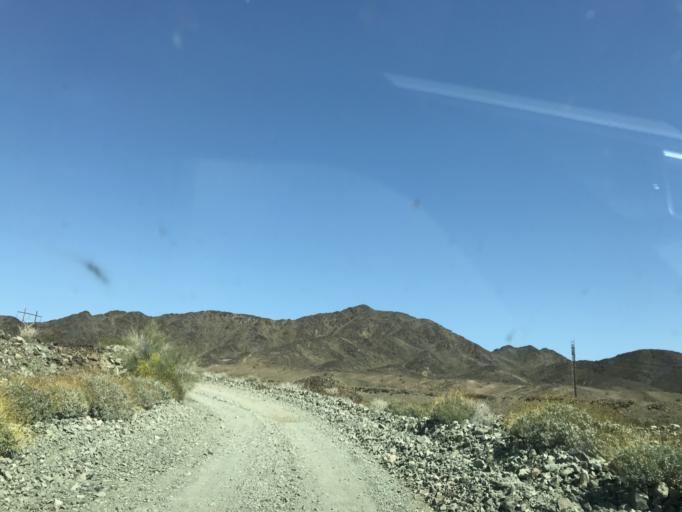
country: US
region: California
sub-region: Riverside County
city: Mesa Verde
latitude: 33.4953
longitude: -114.8351
